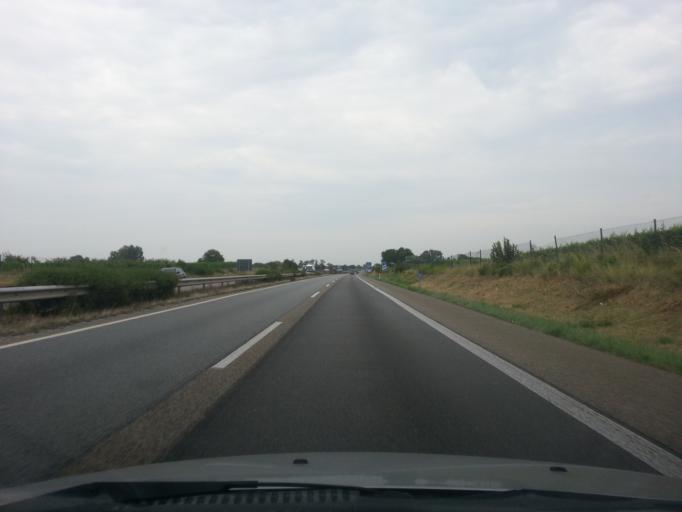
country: DE
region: Rheinland-Pfalz
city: Venningen
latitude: 49.2762
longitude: 8.1531
